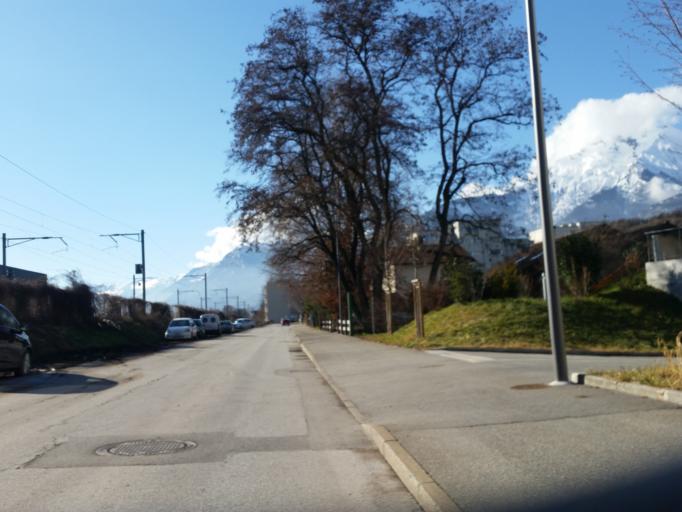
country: CH
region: Valais
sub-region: Sion District
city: Sitten
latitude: 46.2224
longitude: 7.3341
